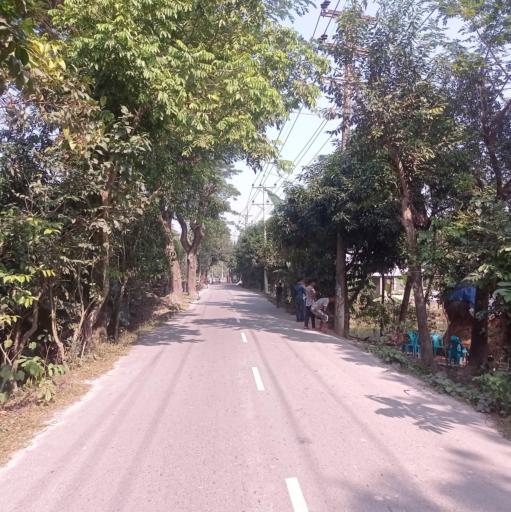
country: BD
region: Dhaka
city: Narsingdi
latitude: 24.0630
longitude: 90.6895
